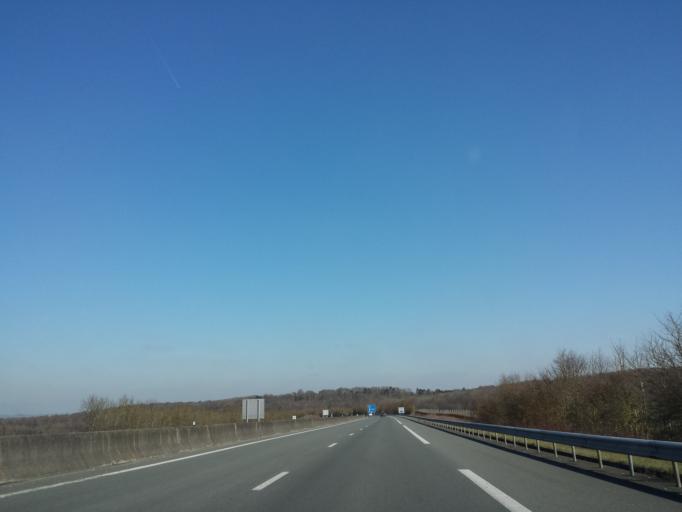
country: FR
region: Picardie
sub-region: Departement de la Somme
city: Saleux
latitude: 49.8247
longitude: 2.2500
